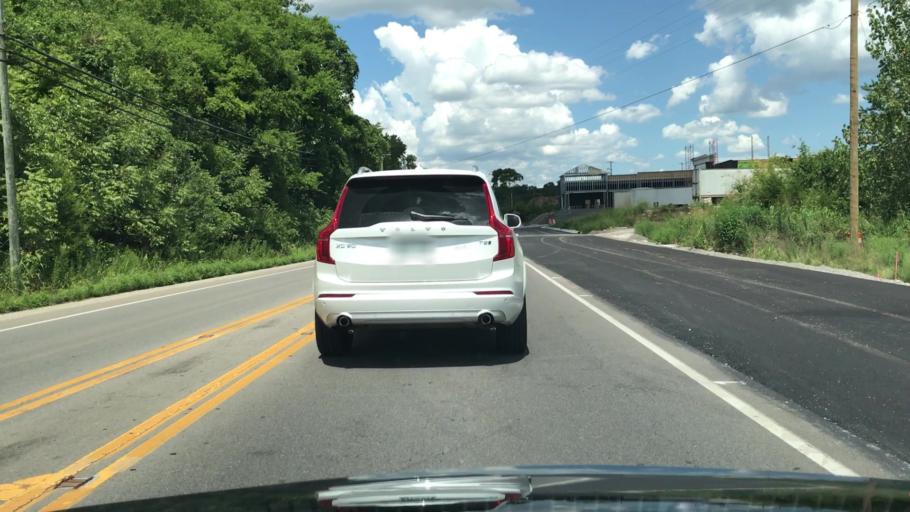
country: US
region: Tennessee
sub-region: Williamson County
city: Nolensville
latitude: 35.9874
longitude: -86.6807
